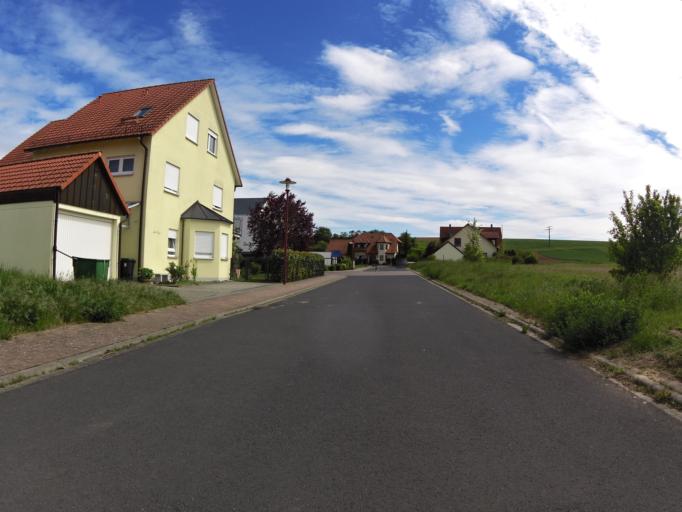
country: DE
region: Bavaria
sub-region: Regierungsbezirk Unterfranken
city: Kurnach
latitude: 49.8410
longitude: 10.0388
